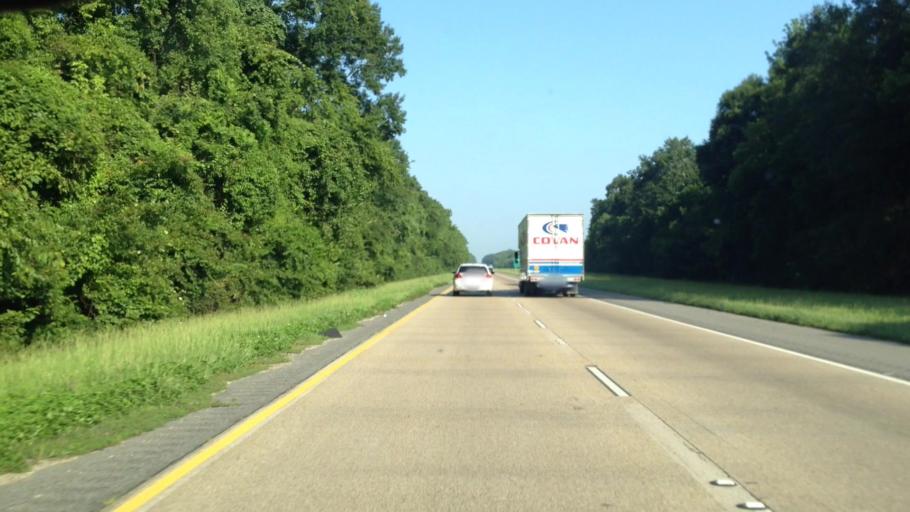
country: US
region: Louisiana
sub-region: Ascension Parish
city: Sorrento
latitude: 30.1799
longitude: -90.8937
